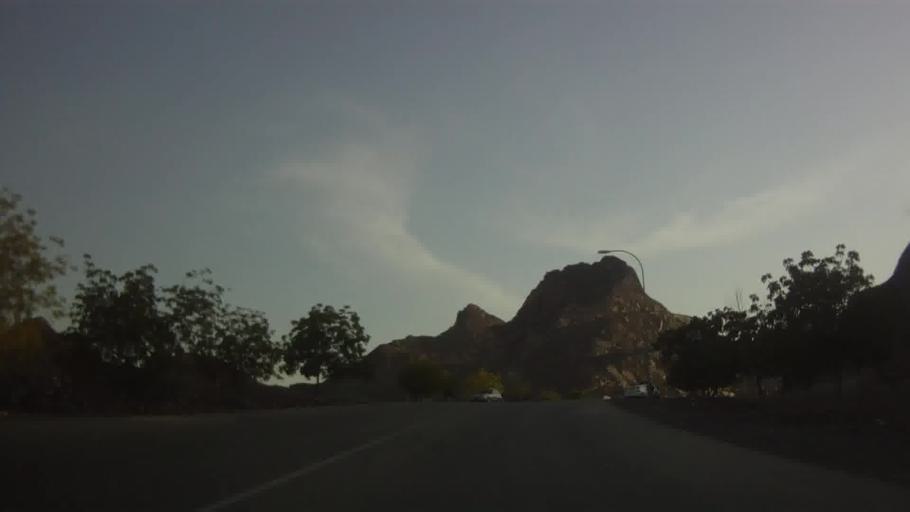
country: OM
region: Muhafazat Masqat
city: Muscat
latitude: 23.5901
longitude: 58.6028
